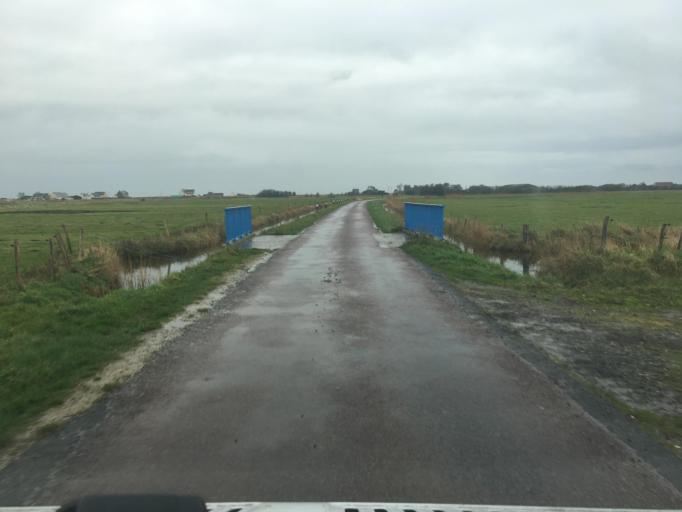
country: FR
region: Lower Normandy
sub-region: Departement de la Manche
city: Sainte-Mere-Eglise
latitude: 49.4499
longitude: -1.2294
